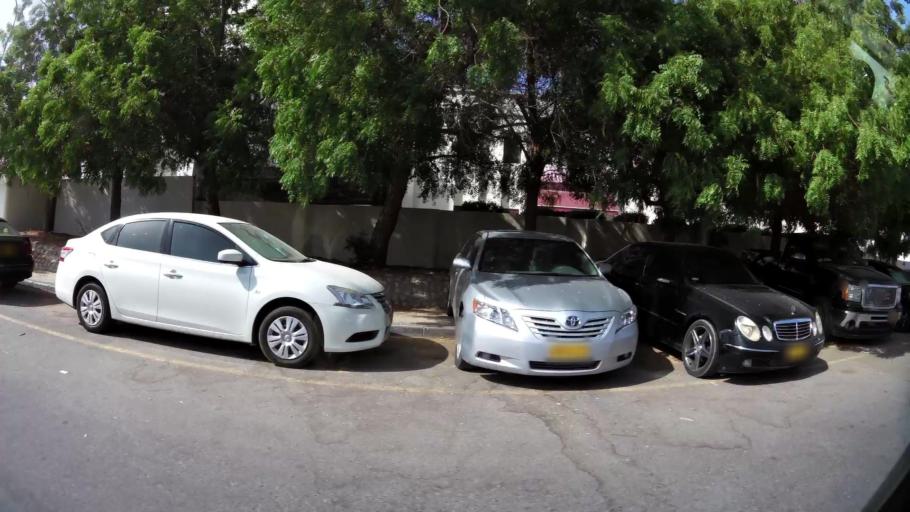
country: OM
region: Muhafazat Masqat
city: Muscat
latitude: 23.6106
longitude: 58.5126
